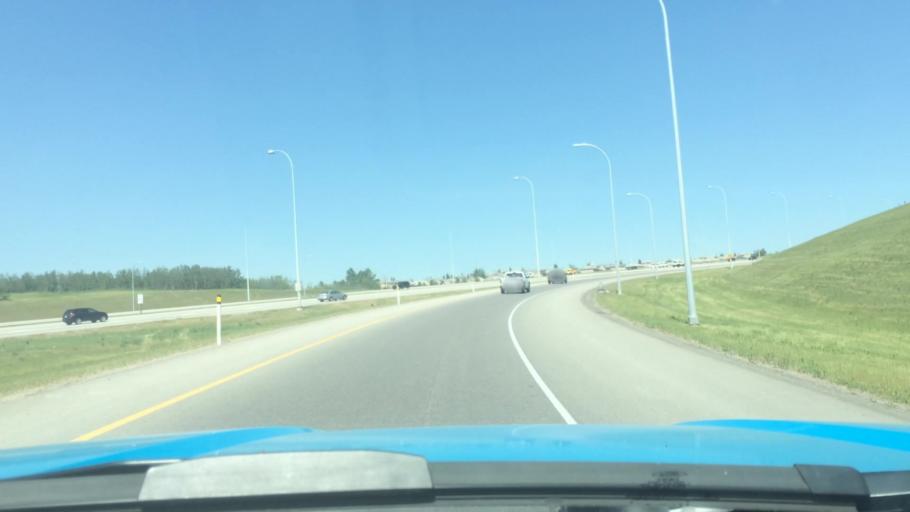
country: CA
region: Alberta
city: Calgary
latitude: 51.1330
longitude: -114.2234
